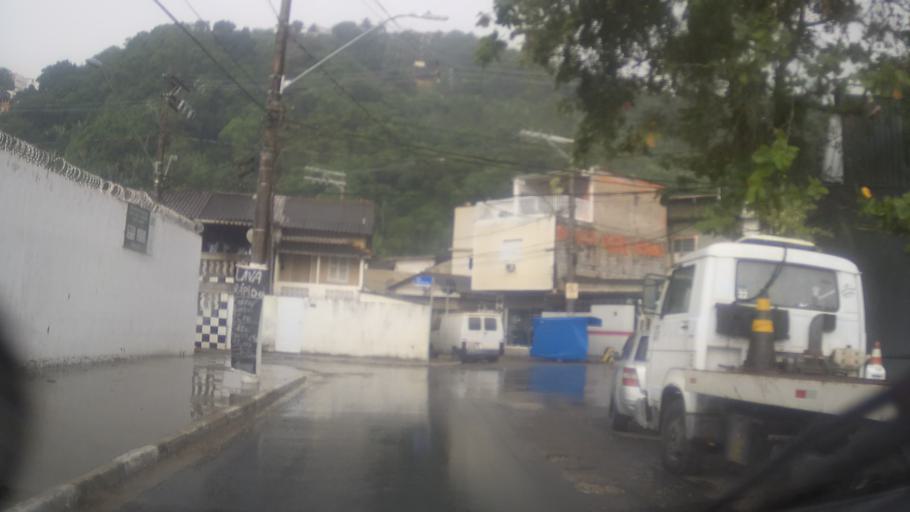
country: BR
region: Sao Paulo
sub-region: Santos
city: Santos
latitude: -23.9344
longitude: -46.3461
